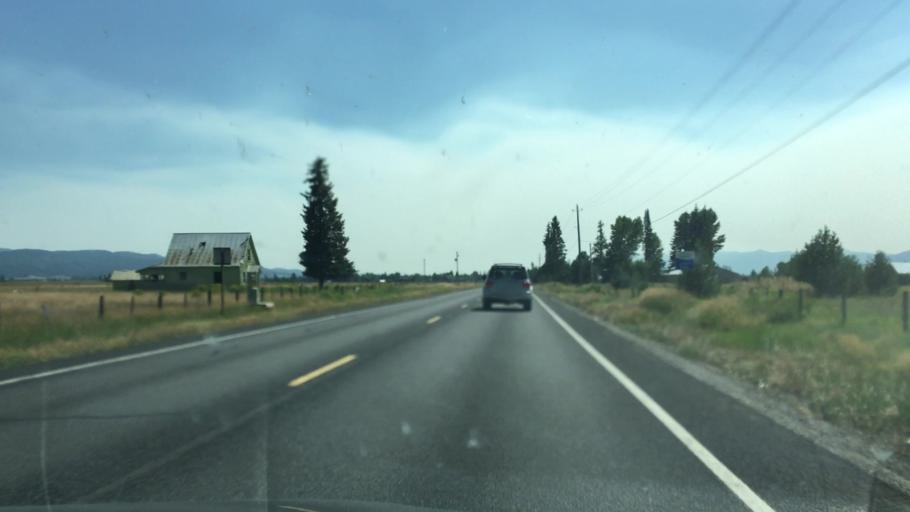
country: US
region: Idaho
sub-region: Valley County
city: McCall
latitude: 44.7485
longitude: -116.0784
